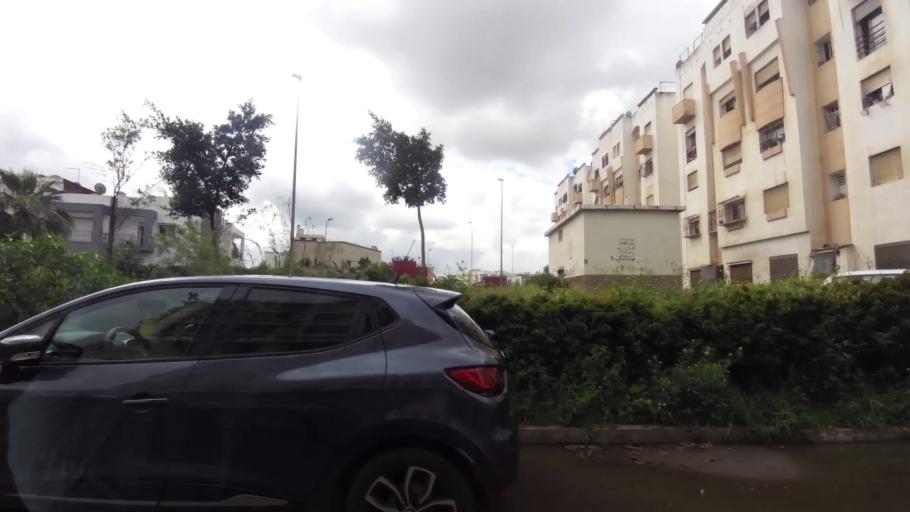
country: MA
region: Grand Casablanca
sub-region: Nouaceur
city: Bouskoura
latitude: 33.5212
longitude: -7.6436
